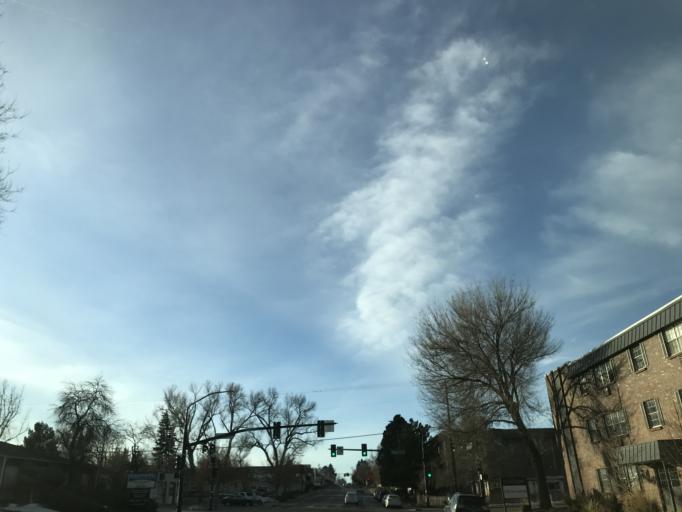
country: US
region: Colorado
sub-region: Arapahoe County
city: Littleton
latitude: 39.6157
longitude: -105.0069
